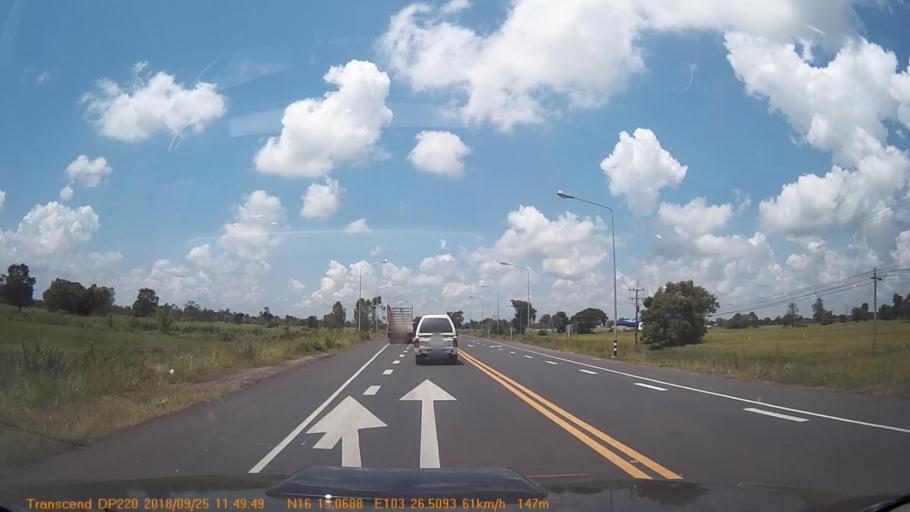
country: TH
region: Kalasin
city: Khong Chai
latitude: 16.3178
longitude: 103.4418
